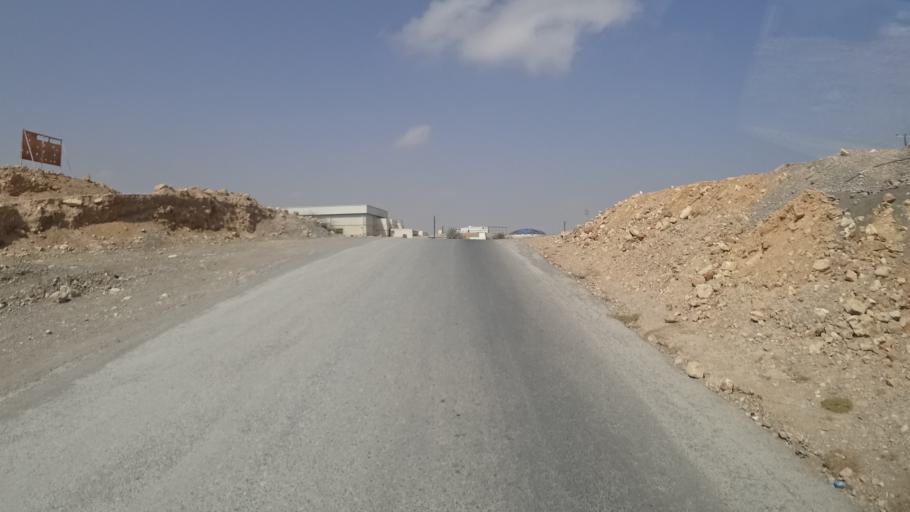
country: OM
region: Muhafazat Masqat
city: Bawshar
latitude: 23.5642
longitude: 58.3431
